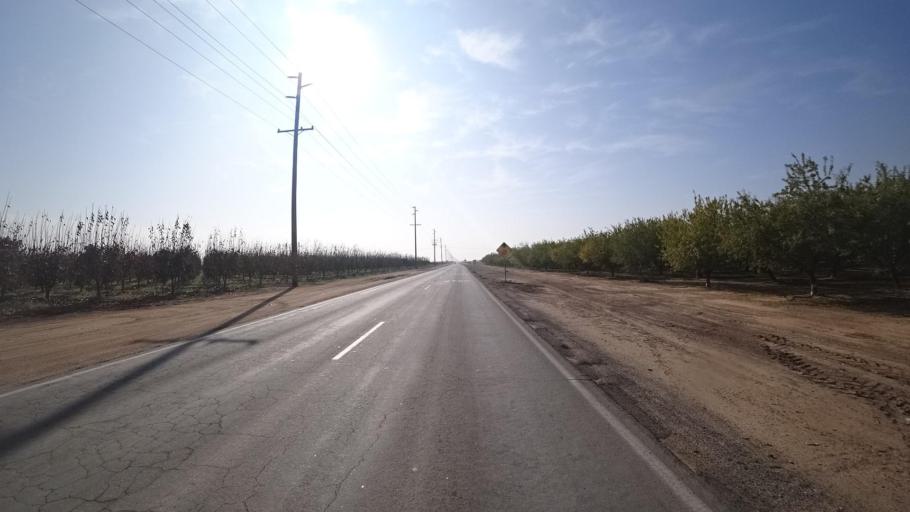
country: US
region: California
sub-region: Kern County
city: Delano
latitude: 35.7490
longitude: -119.2233
